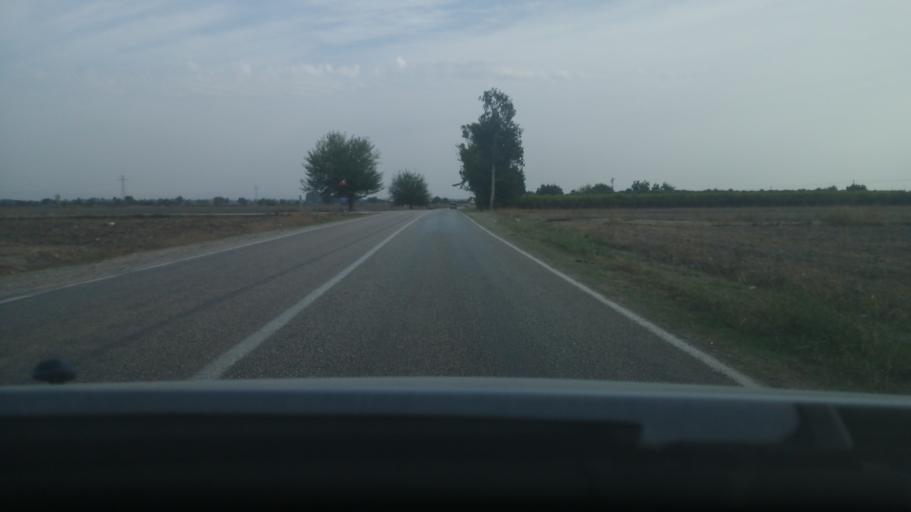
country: TR
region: Adana
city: Kozan
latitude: 37.3592
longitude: 35.8728
